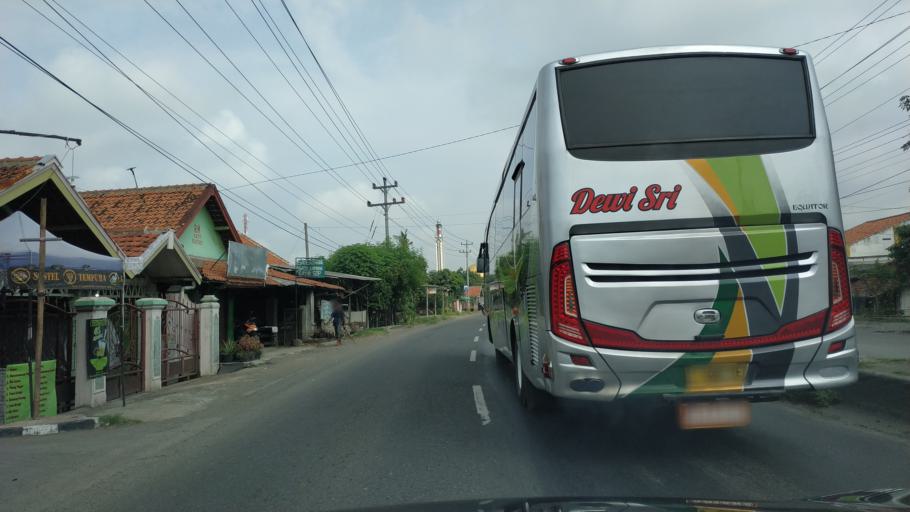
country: ID
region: Central Java
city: Bulakamba
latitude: -6.8748
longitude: 108.9189
